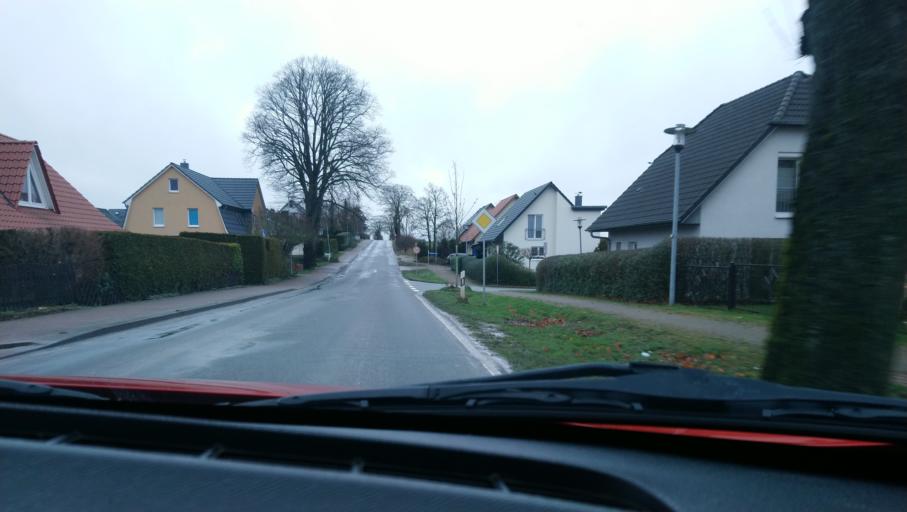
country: DE
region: Mecklenburg-Vorpommern
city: Seehof
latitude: 53.6846
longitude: 11.4296
